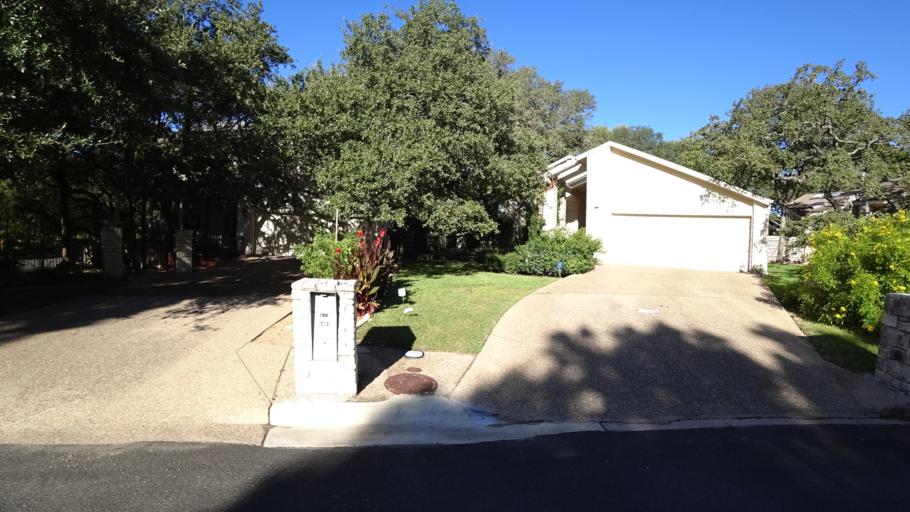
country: US
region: Texas
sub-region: Travis County
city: West Lake Hills
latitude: 30.3552
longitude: -97.7886
